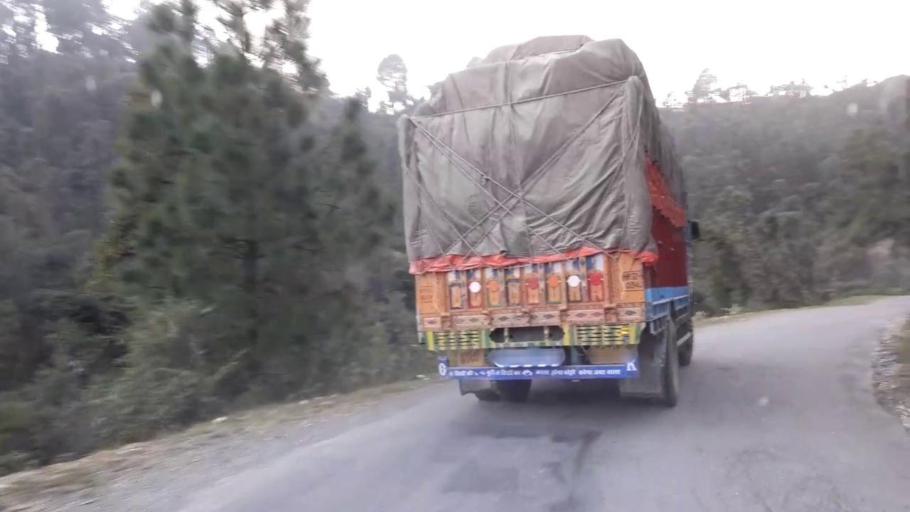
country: IN
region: Himachal Pradesh
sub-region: Shimla
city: Shimla
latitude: 31.0513
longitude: 77.1486
